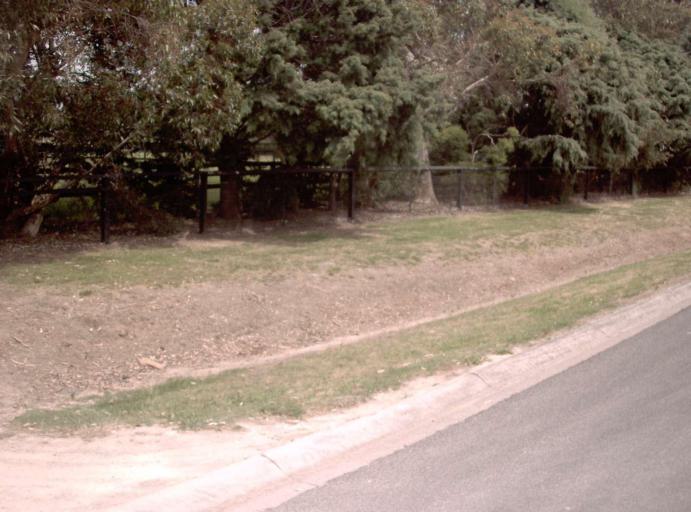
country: AU
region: Victoria
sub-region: Mornington Peninsula
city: Moorooduc
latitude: -38.2508
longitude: 145.0813
